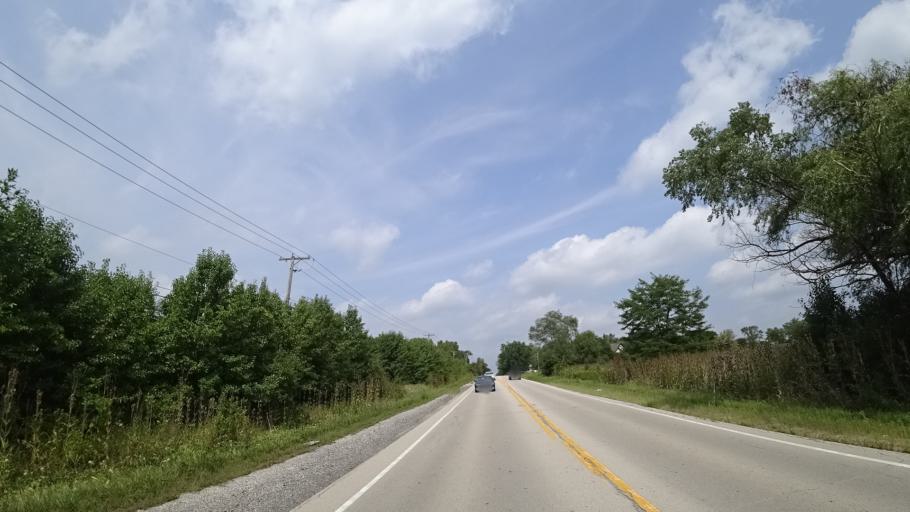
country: US
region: Illinois
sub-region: Cook County
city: Orland Park
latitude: 41.6238
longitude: -87.8922
